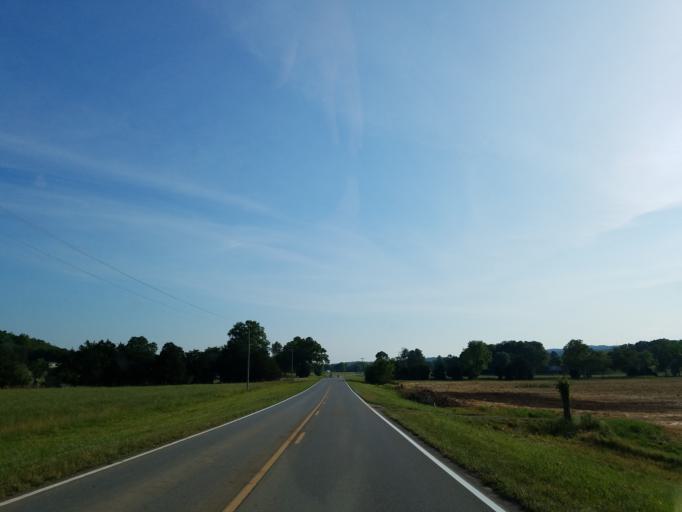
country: US
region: Georgia
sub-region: Chattooga County
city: Trion
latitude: 34.4891
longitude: -85.2519
